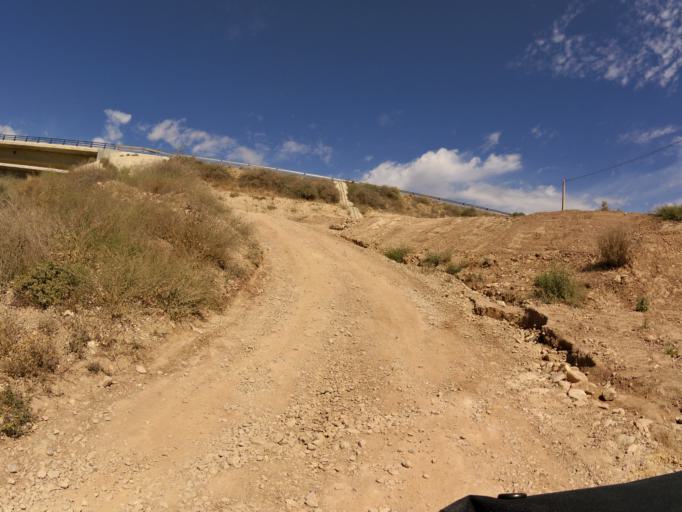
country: ES
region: Valencia
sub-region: Provincia de Alicante
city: Agost
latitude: 38.3973
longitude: -0.6088
